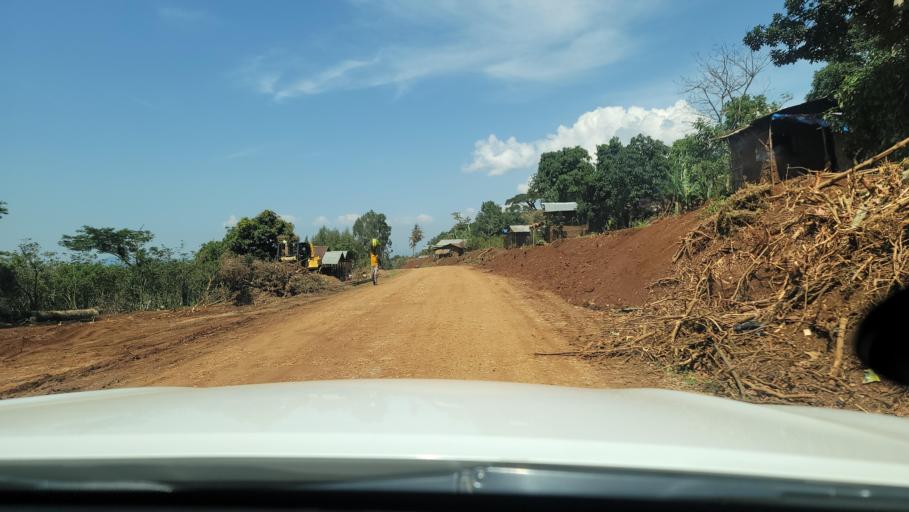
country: ET
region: Oromiya
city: Agaro
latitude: 7.8049
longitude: 36.4611
